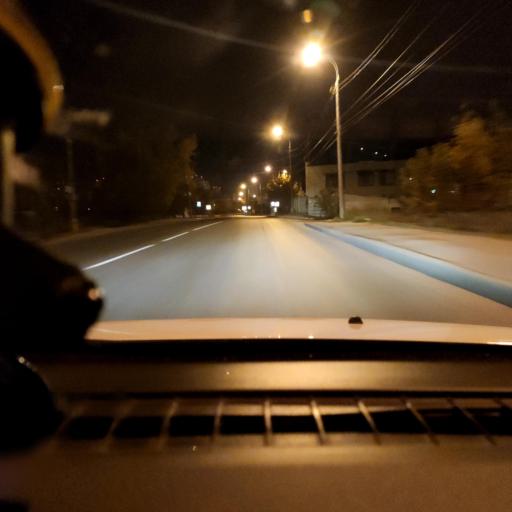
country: RU
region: Samara
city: Rozhdestveno
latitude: 53.1624
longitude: 50.0761
